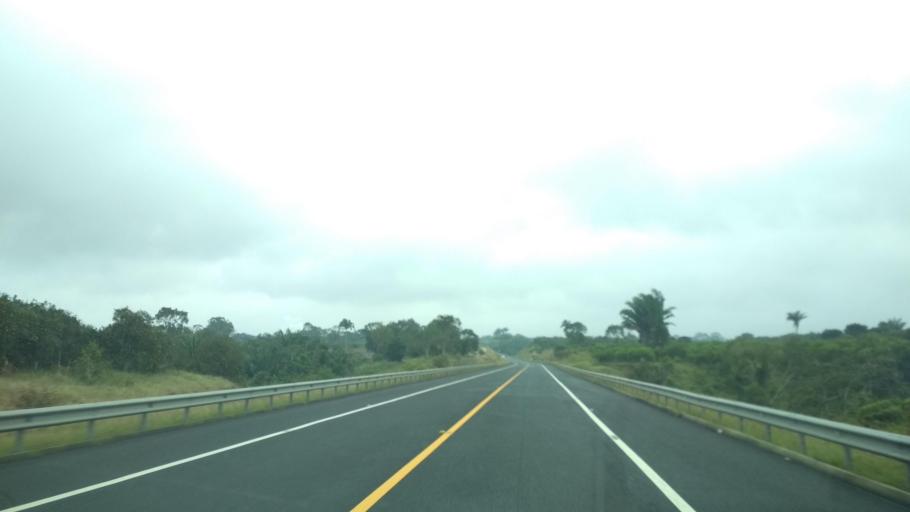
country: MX
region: Veracruz
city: Vega de San Marcos
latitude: 20.1832
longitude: -96.9662
